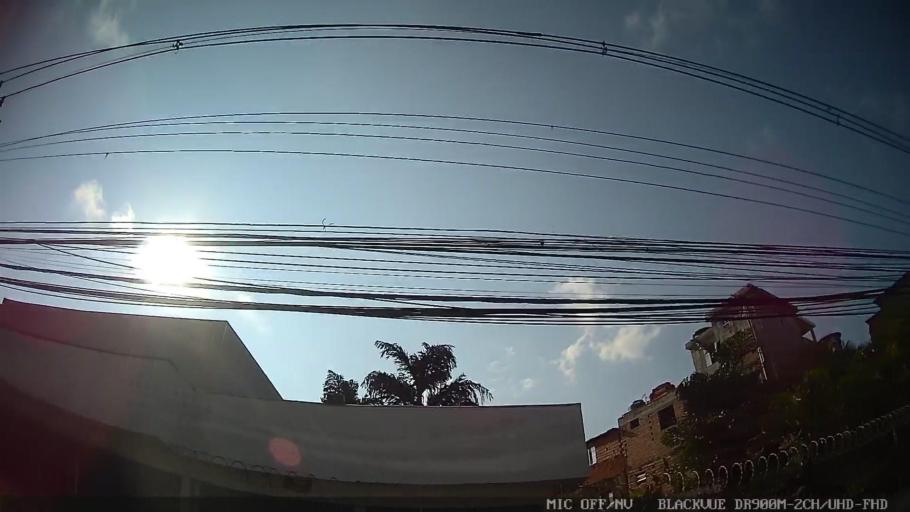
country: BR
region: Sao Paulo
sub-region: Taboao Da Serra
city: Taboao da Serra
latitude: -23.6105
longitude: -46.7274
